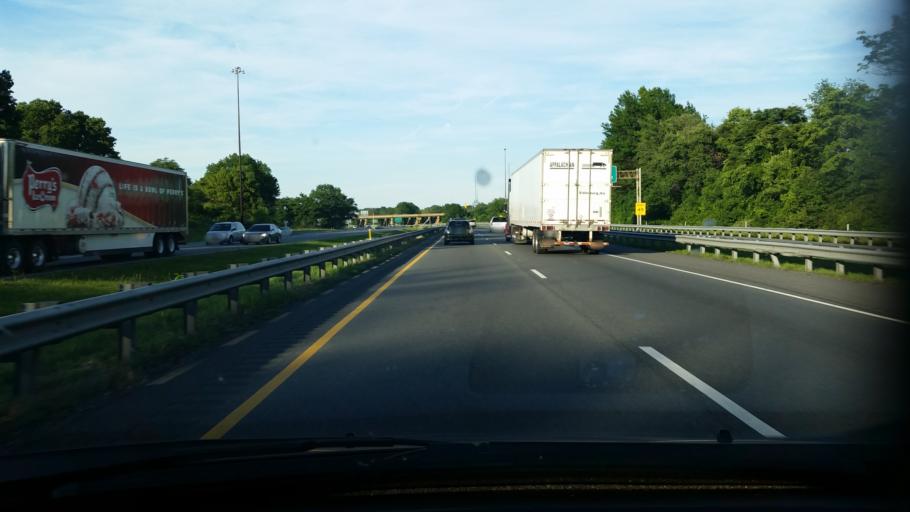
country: US
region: Maryland
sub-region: Washington County
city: Williamsport
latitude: 39.6153
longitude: -77.7914
